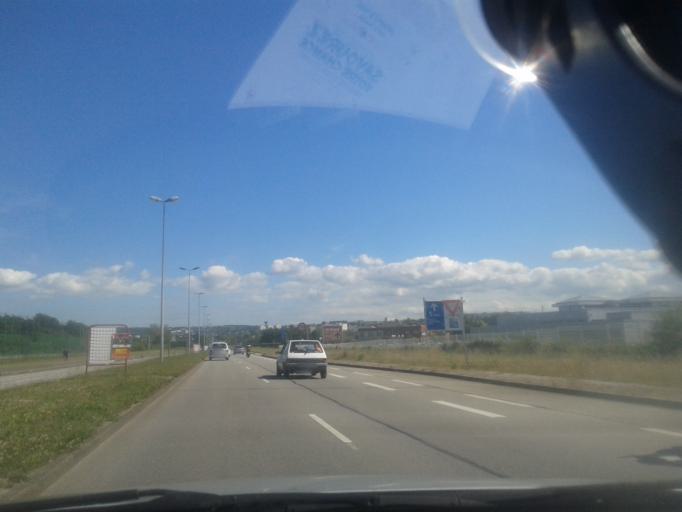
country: FR
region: Lower Normandy
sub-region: Departement de la Manche
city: Equeurdreville-Hainneville
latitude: 49.6532
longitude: -1.6485
